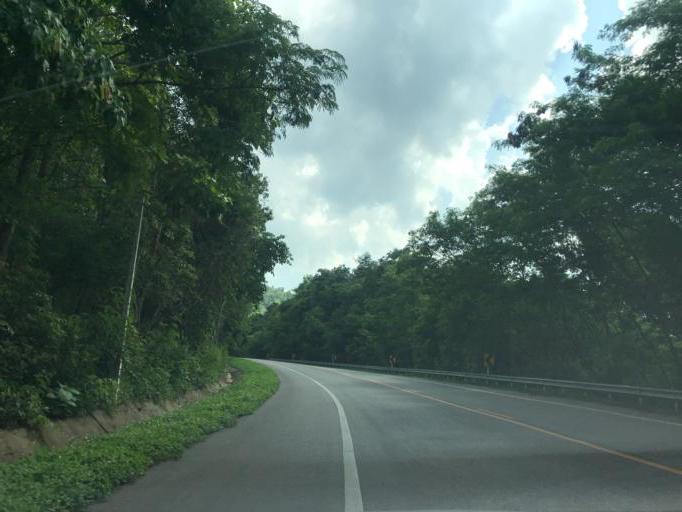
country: TH
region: Phayao
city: Phayao
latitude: 19.0884
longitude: 99.8217
